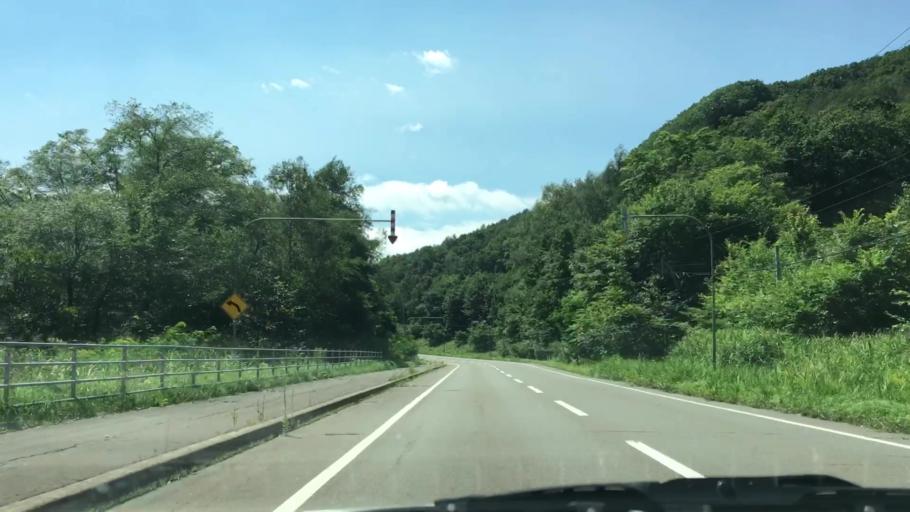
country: JP
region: Hokkaido
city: Otofuke
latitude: 43.2548
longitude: 143.5676
